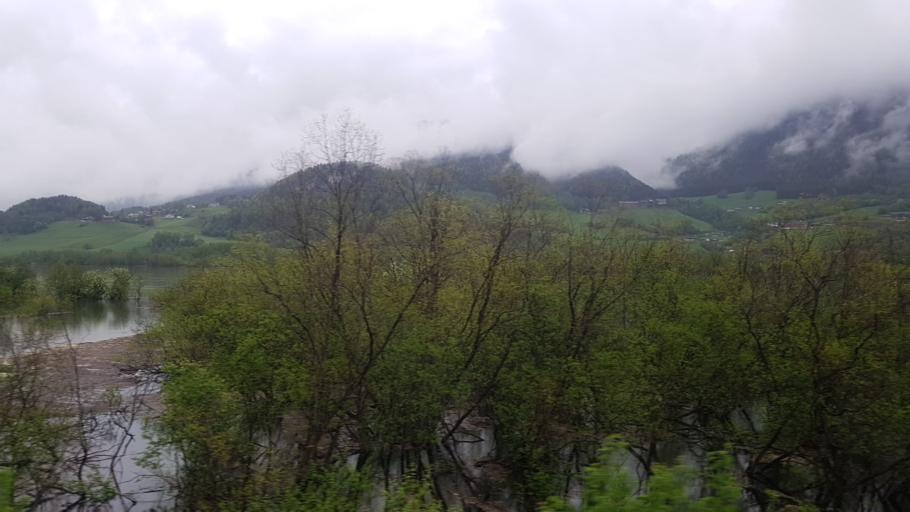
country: NO
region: Oppland
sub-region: Oyer
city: Tretten
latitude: 61.4047
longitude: 10.2380
